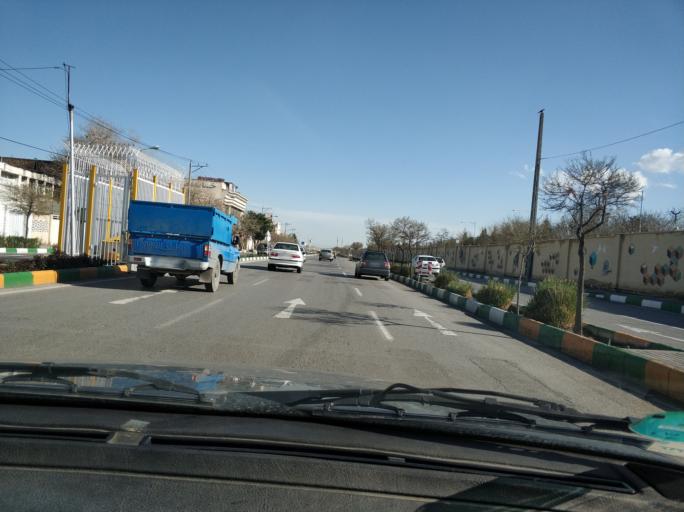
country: IR
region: Razavi Khorasan
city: Mashhad
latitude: 36.3106
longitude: 59.6240
